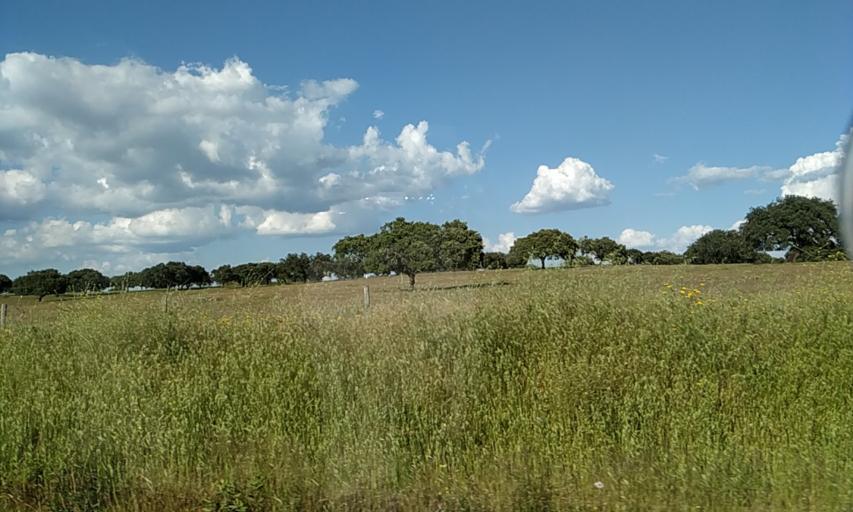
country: PT
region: Portalegre
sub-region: Portalegre
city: Urra
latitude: 39.1408
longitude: -7.4508
